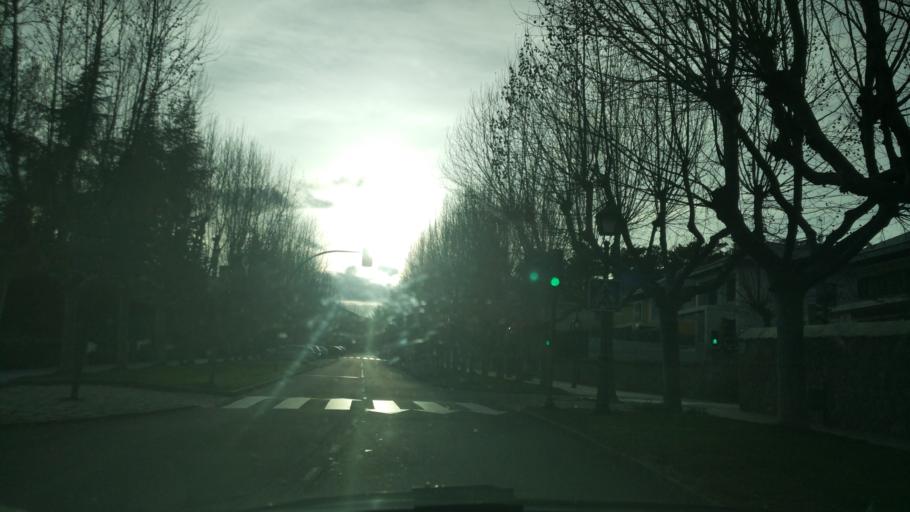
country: ES
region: Madrid
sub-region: Provincia de Madrid
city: El Escorial
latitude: 40.5822
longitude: -4.1245
